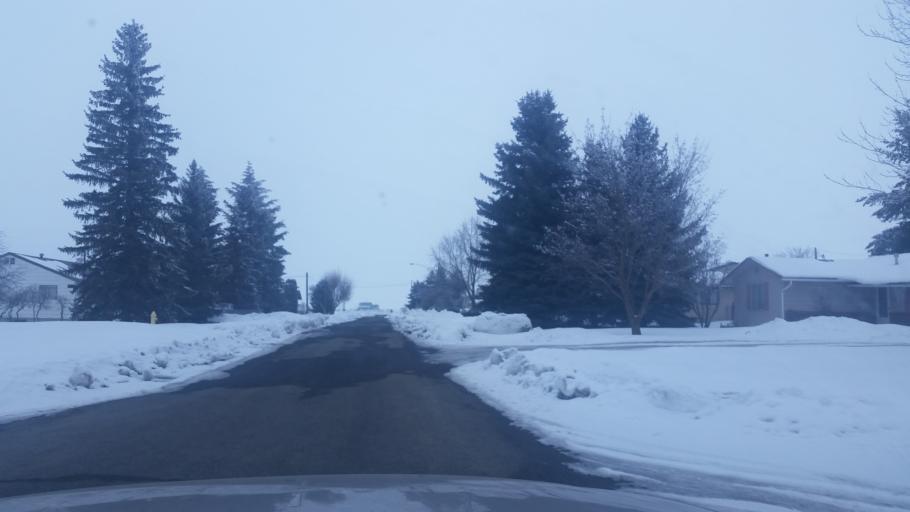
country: US
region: Washington
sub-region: Spokane County
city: Medical Lake
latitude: 47.6684
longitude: -117.8717
